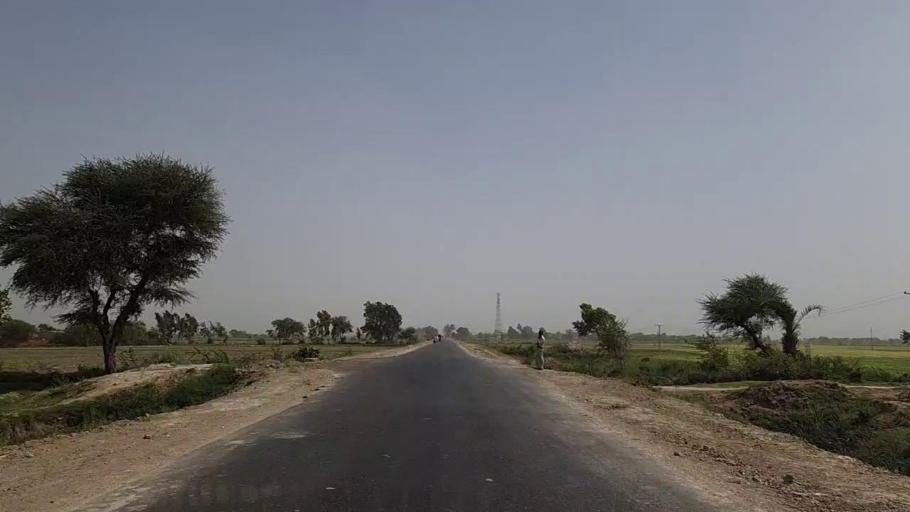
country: PK
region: Sindh
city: Tando Bago
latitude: 24.8202
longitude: 68.9036
